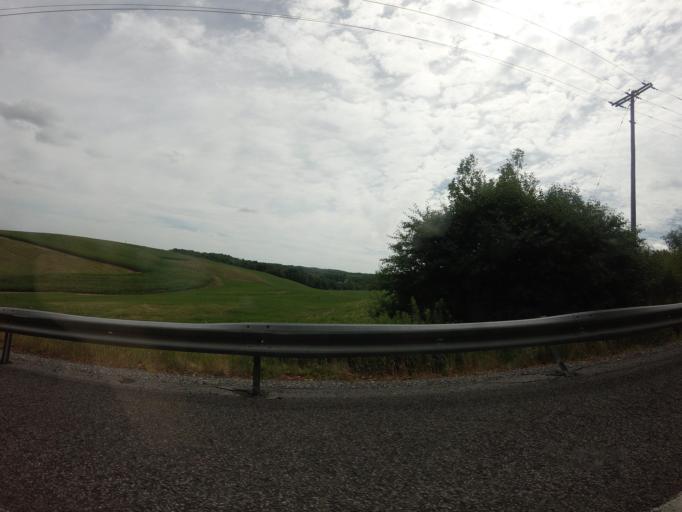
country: US
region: New York
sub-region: Onondaga County
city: Camillus
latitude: 43.0267
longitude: -76.3040
